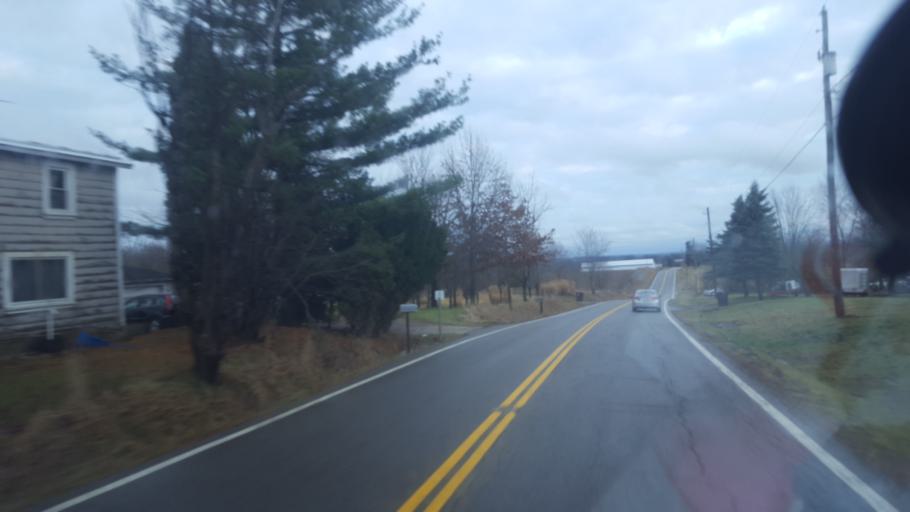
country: US
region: Ohio
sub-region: Sandusky County
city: Bellville
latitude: 40.5642
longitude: -82.5649
